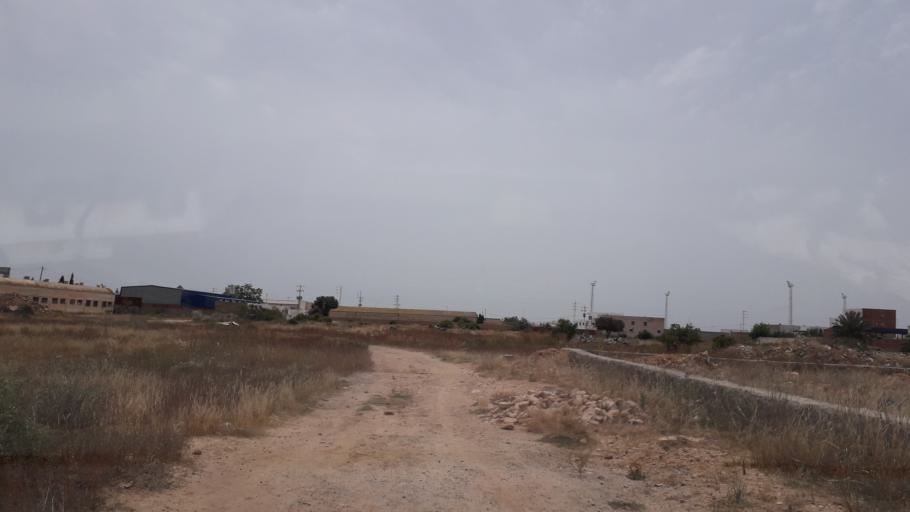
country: TN
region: Safaqis
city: Al Qarmadah
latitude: 34.8468
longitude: 10.7572
